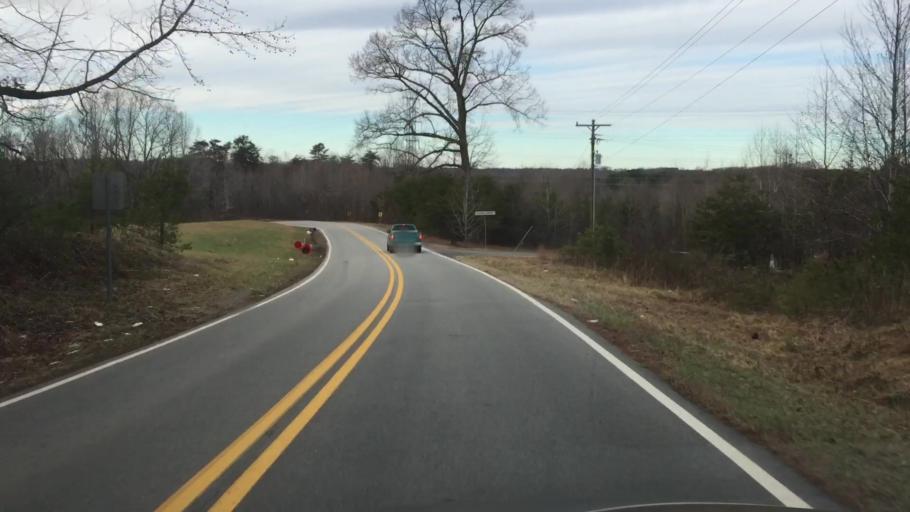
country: US
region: North Carolina
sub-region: Rockingham County
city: Reidsville
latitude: 36.3929
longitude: -79.6566
